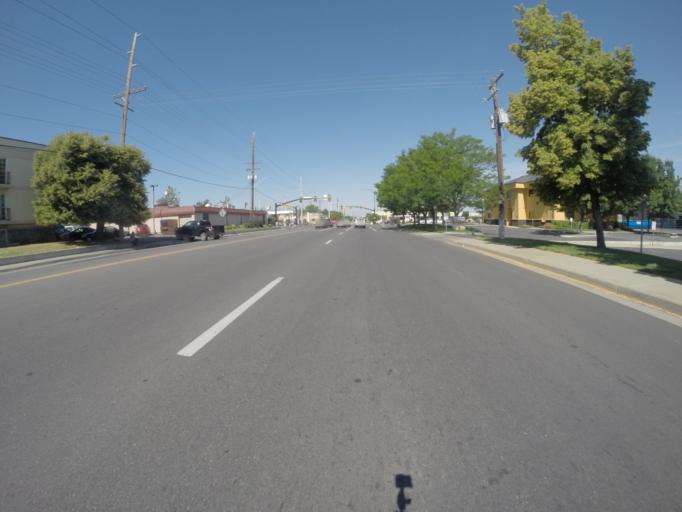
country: US
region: Utah
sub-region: Salt Lake County
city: Salt Lake City
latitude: 40.7417
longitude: -111.8871
